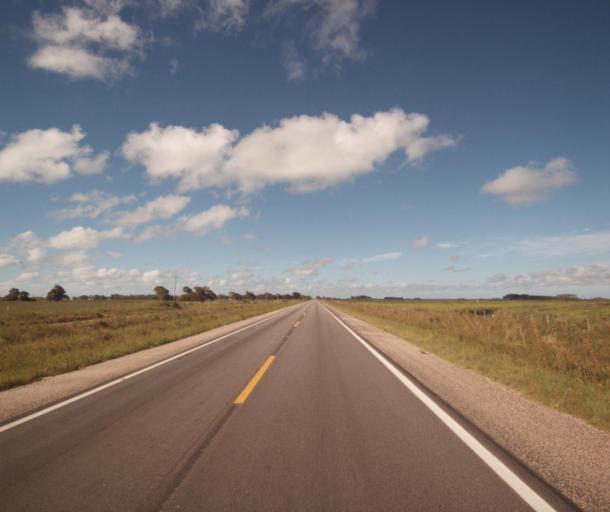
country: UY
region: Cerro Largo
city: Rio Branco
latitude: -32.9539
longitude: -52.7791
